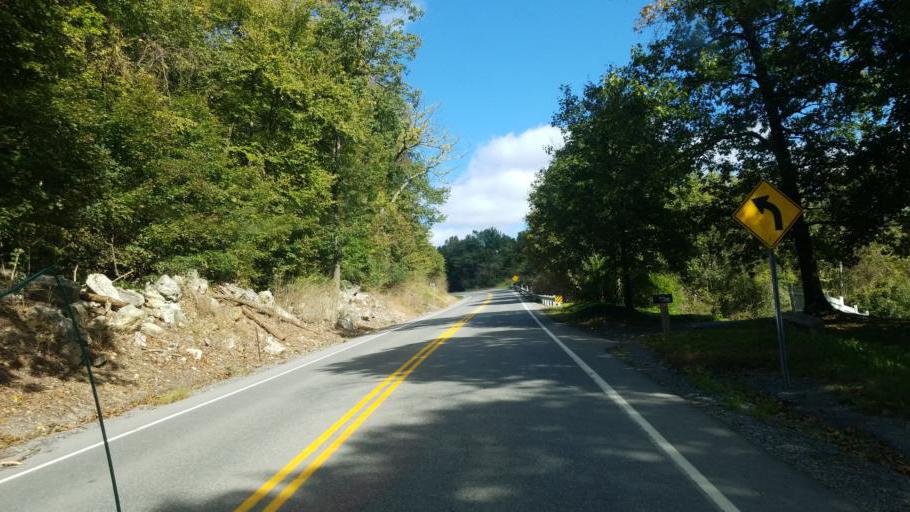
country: US
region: Pennsylvania
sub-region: Fulton County
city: McConnellsburg
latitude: 39.9351
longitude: -78.0162
